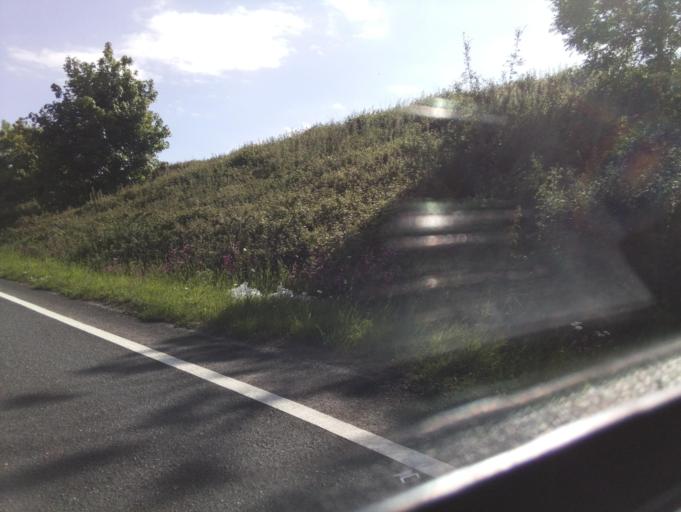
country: GB
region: England
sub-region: Devon
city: Marldon
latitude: 50.4747
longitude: -3.5832
